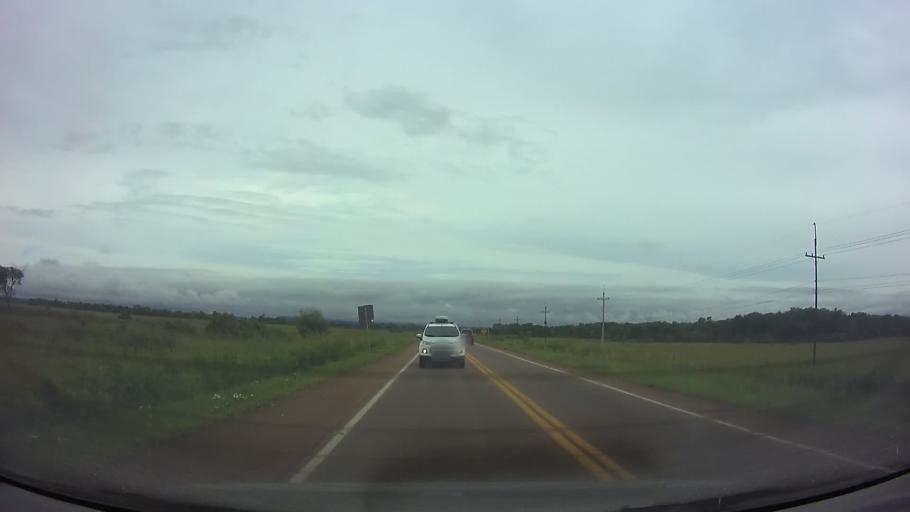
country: PY
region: Paraguari
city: Carapegua
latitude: -25.7205
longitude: -57.2013
